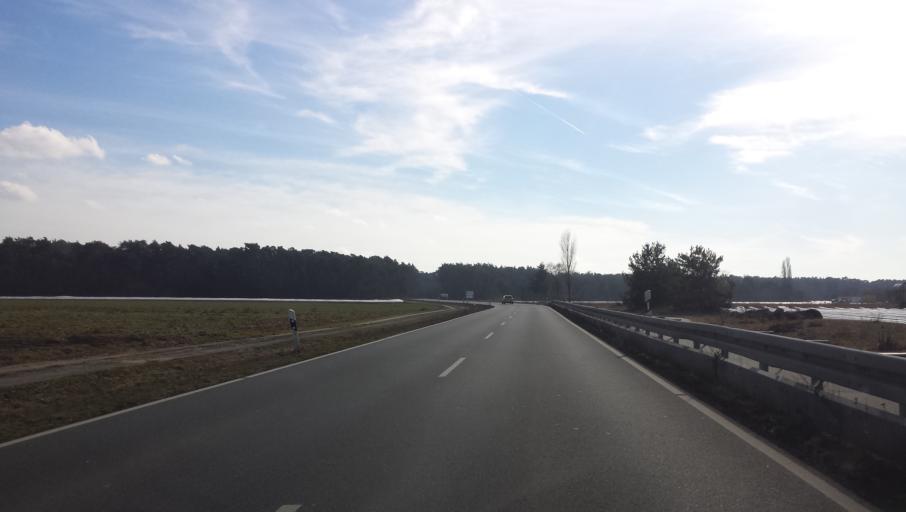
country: DE
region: Hesse
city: Weiterstadt
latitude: 49.9190
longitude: 8.6153
